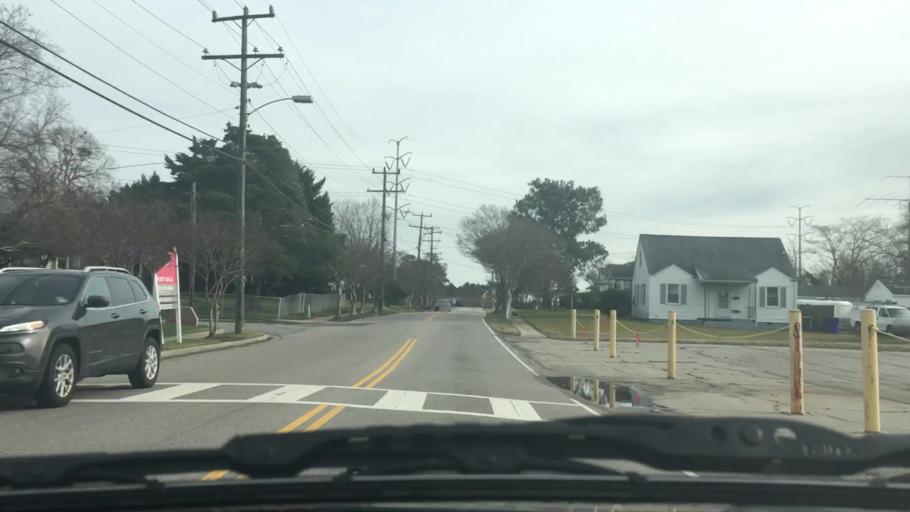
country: US
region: Virginia
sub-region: City of Norfolk
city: Norfolk
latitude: 36.8914
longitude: -76.2567
